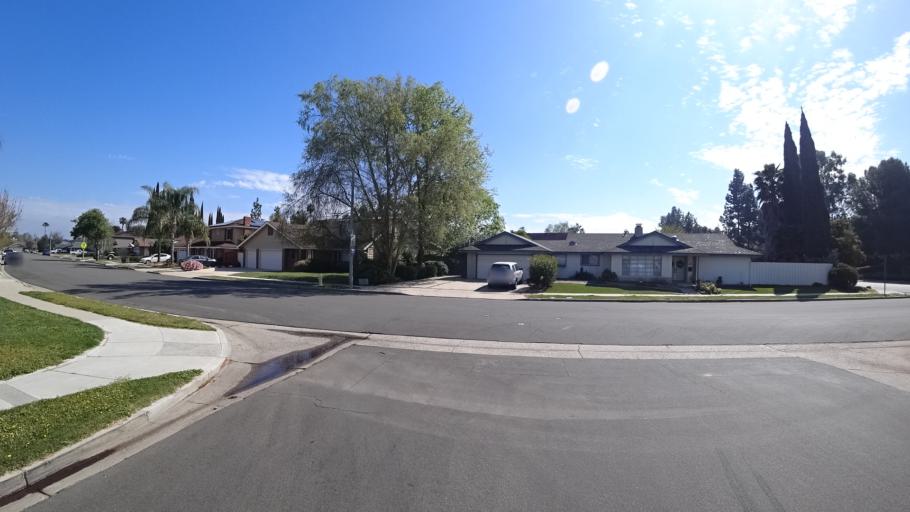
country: US
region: California
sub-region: Ventura County
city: Casa Conejo
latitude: 34.1803
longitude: -118.9316
